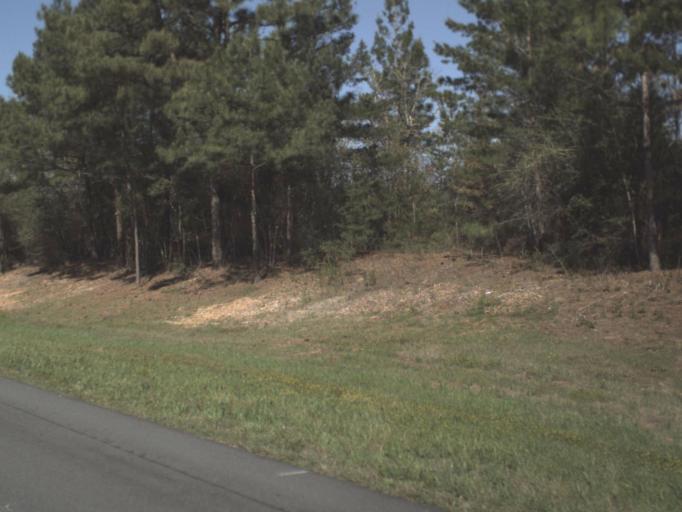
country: US
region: Florida
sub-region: Walton County
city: DeFuniak Springs
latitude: 30.6954
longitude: -85.9993
